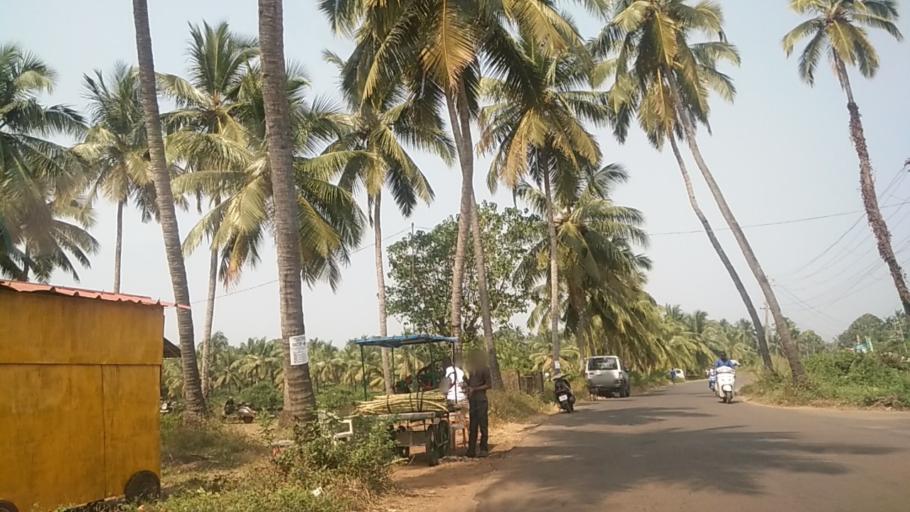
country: IN
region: Goa
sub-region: North Goa
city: Arambol
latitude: 15.6827
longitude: 73.7107
